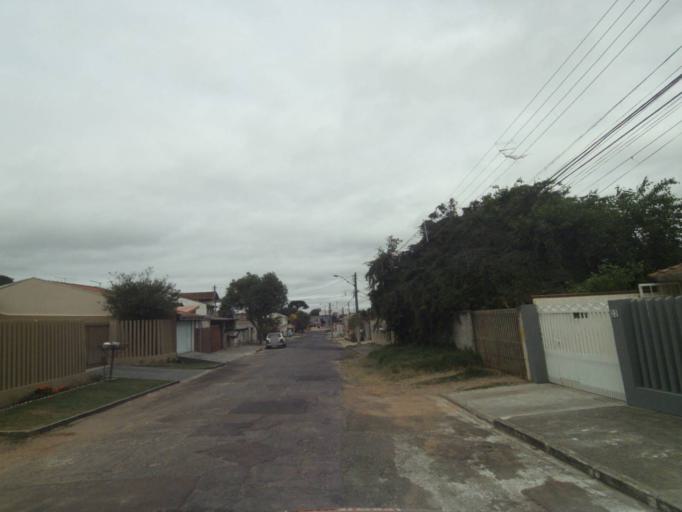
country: BR
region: Parana
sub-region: Sao Jose Dos Pinhais
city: Sao Jose dos Pinhais
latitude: -25.4860
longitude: -49.2332
